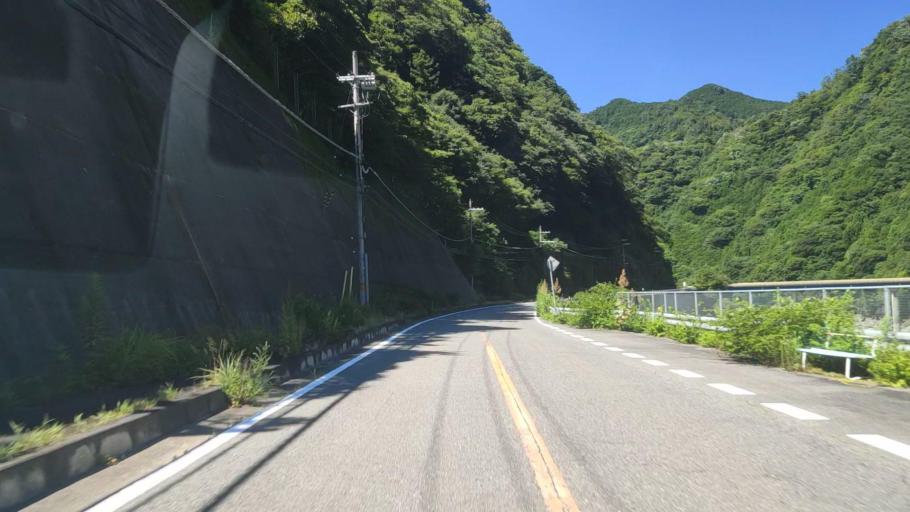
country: JP
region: Nara
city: Yoshino-cho
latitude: 34.3072
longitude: 135.9921
